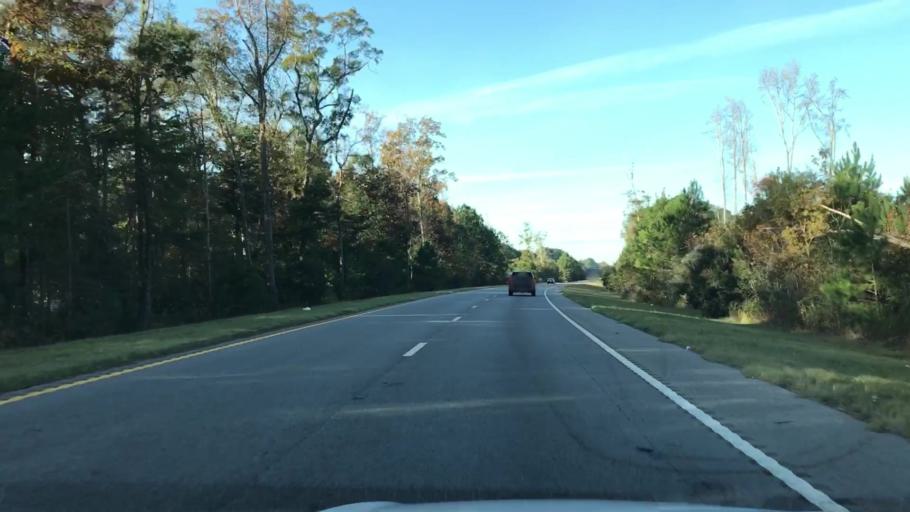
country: US
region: South Carolina
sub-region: Colleton County
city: Walterboro
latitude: 32.7389
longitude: -80.5676
